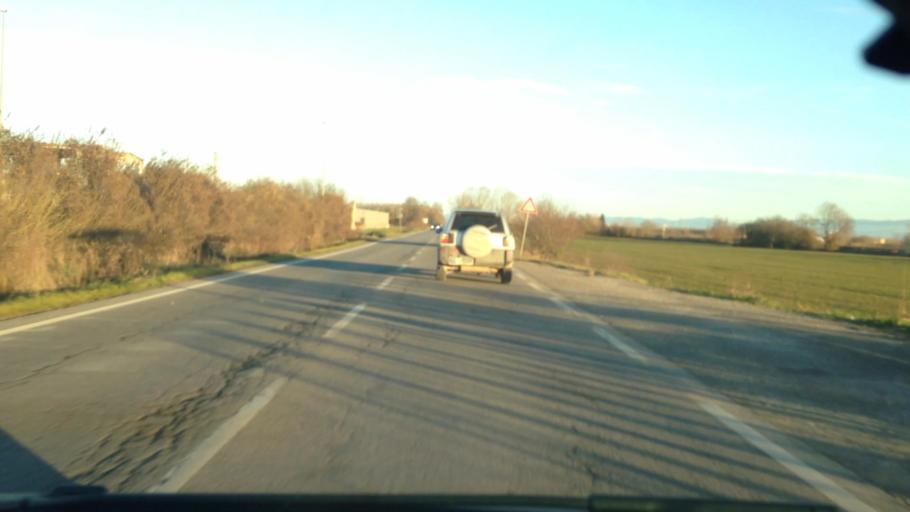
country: IT
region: Piedmont
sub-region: Provincia di Alessandria
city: Solero
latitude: 44.9210
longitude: 8.5273
